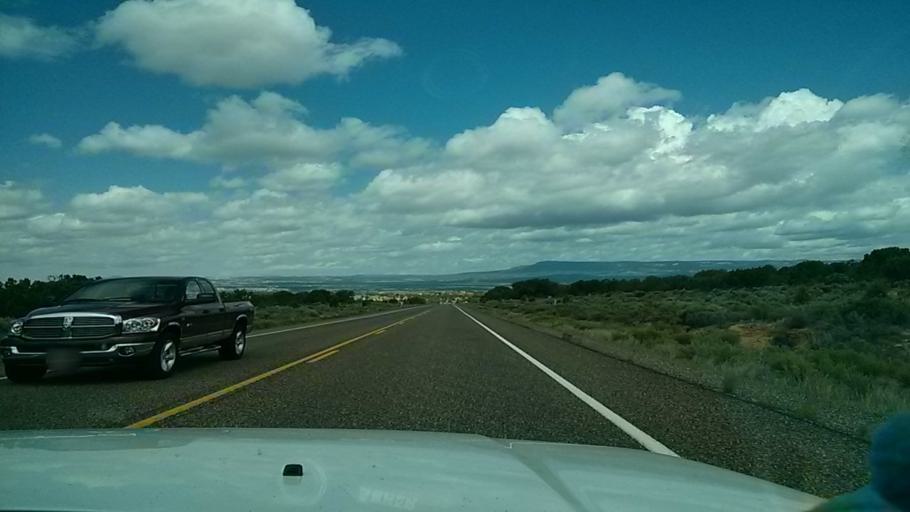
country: US
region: Utah
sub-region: Kane County
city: Kanab
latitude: 37.1826
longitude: -112.6423
